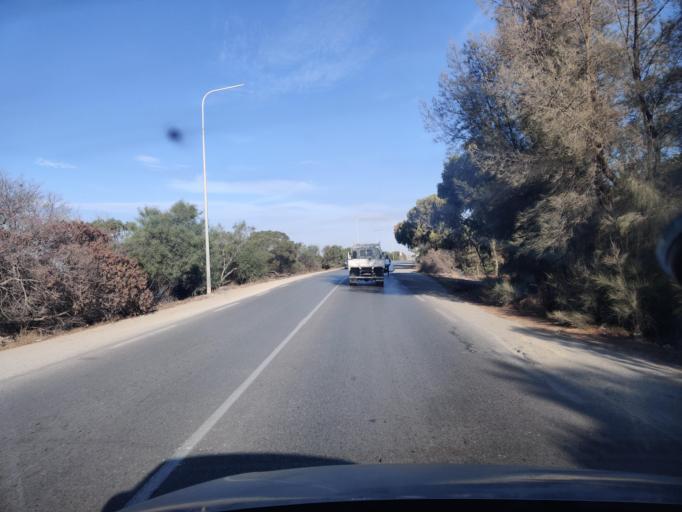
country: TN
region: Tunis
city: Al Marsa
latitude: 36.9404
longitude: 10.2497
